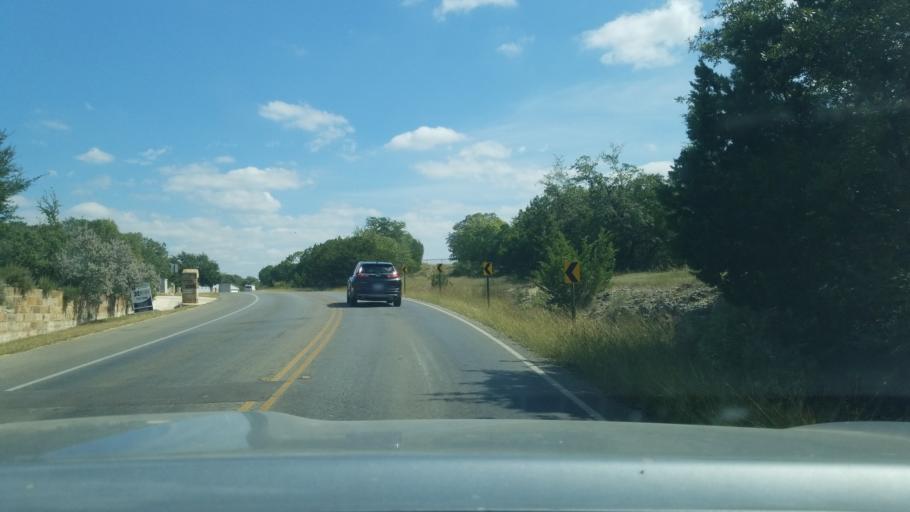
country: US
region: Texas
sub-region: Bexar County
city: Fair Oaks Ranch
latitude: 29.7311
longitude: -98.6360
